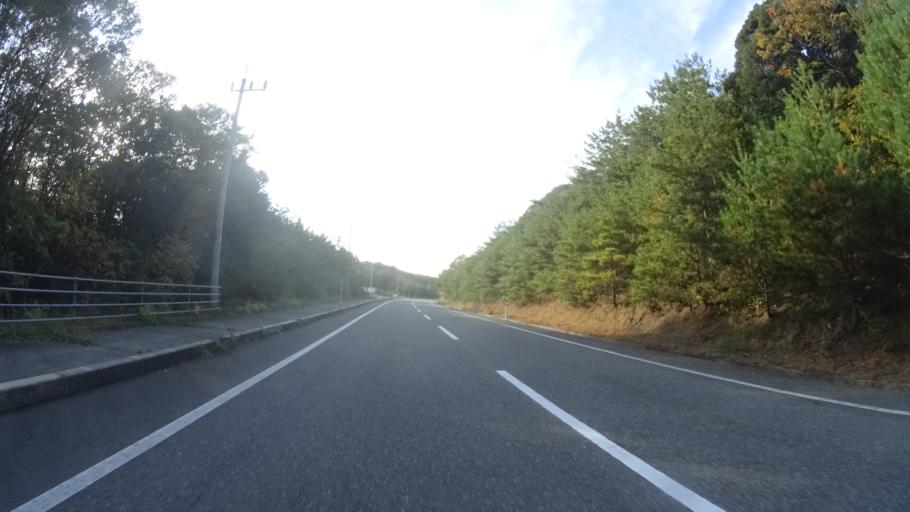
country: JP
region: Ishikawa
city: Hakui
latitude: 37.0710
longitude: 136.7392
